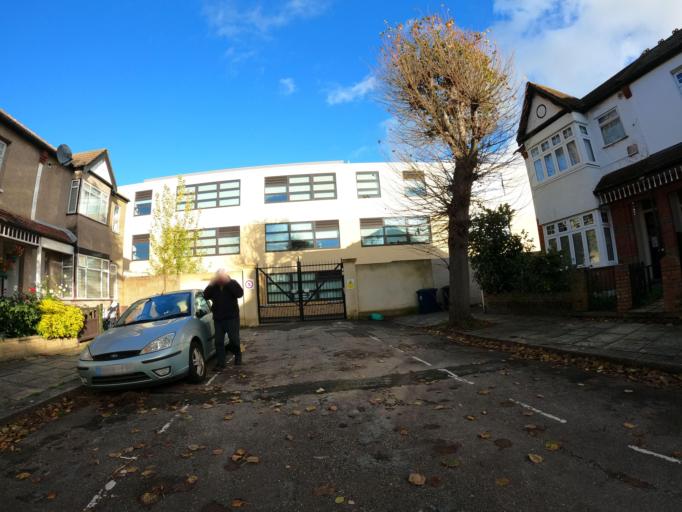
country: GB
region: England
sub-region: Greater London
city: Brentford
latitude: 51.4956
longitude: -0.3128
